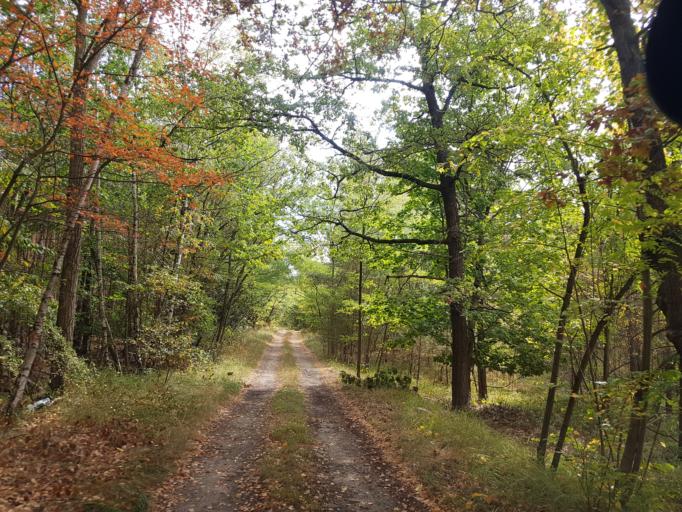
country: DE
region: Brandenburg
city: Finsterwalde
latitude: 51.5967
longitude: 13.7356
